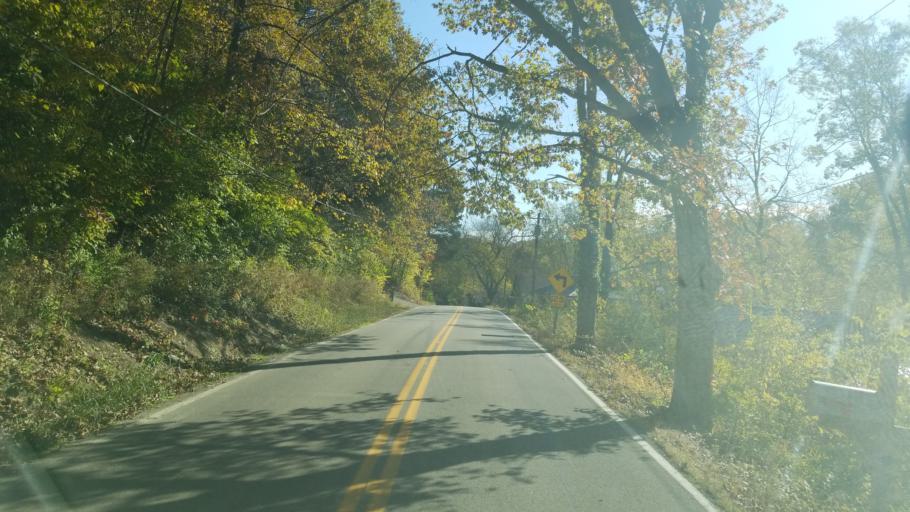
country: US
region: Ohio
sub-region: Warren County
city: Morrow
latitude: 39.3615
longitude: -84.1139
